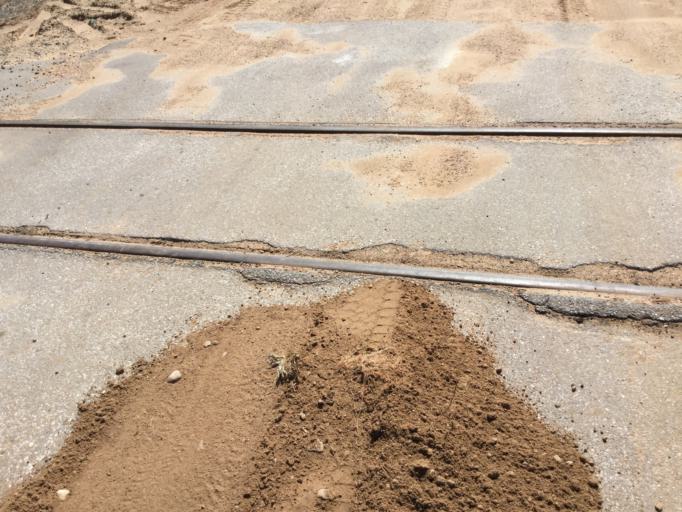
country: US
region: Kansas
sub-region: Barber County
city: Medicine Lodge
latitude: 37.2488
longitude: -98.4595
